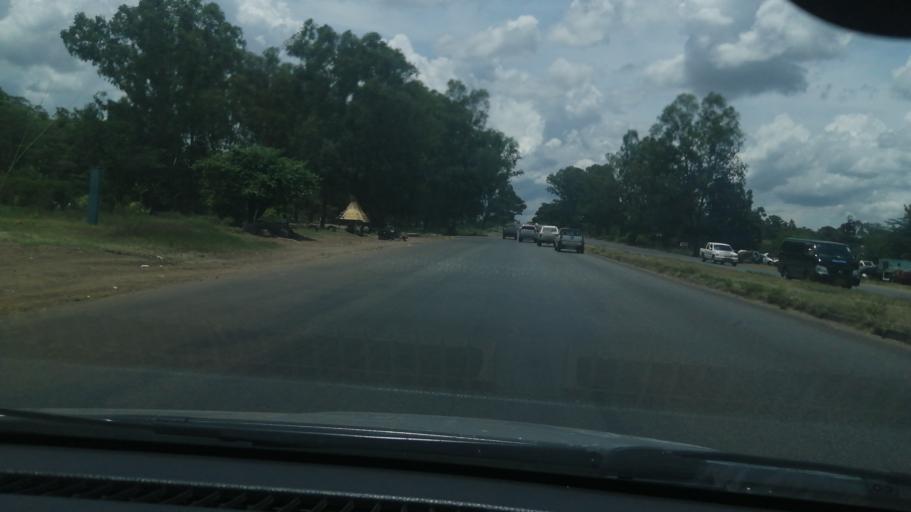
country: ZW
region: Harare
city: Harare
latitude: -17.8215
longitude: 30.9551
